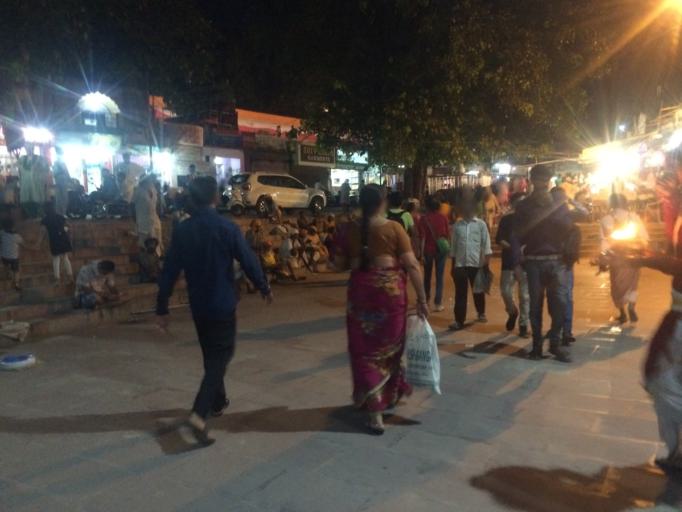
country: IN
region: Uttarakhand
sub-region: Dehradun
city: Rishikesh
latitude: 30.1036
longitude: 78.2993
